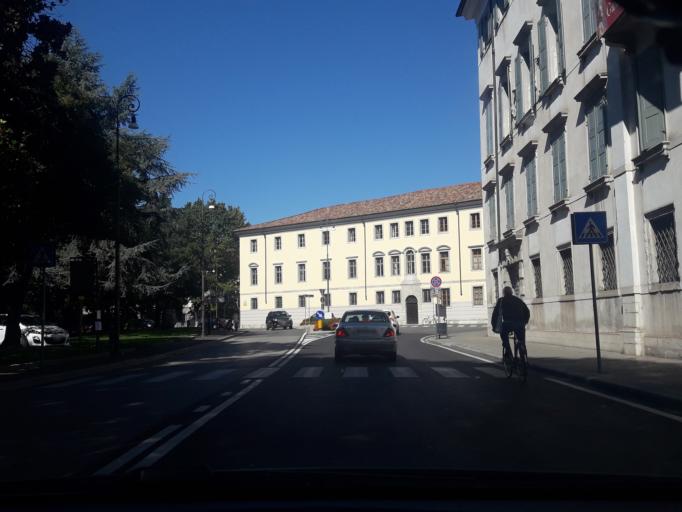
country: IT
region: Friuli Venezia Giulia
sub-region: Provincia di Udine
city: Udine
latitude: 46.0637
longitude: 13.2398
